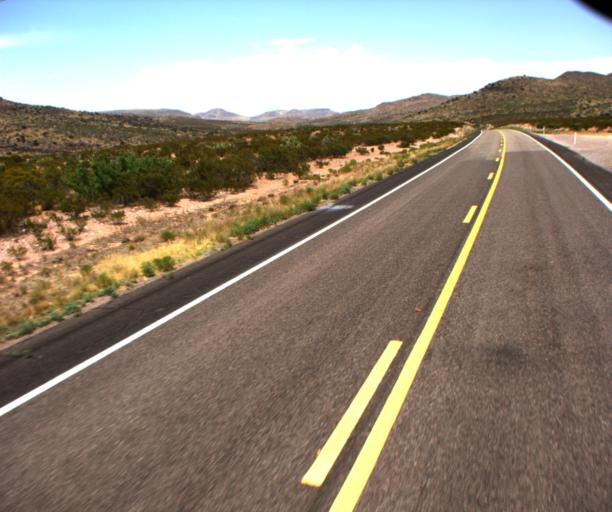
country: US
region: Arizona
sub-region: Greenlee County
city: Clifton
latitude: 32.7525
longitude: -109.3356
